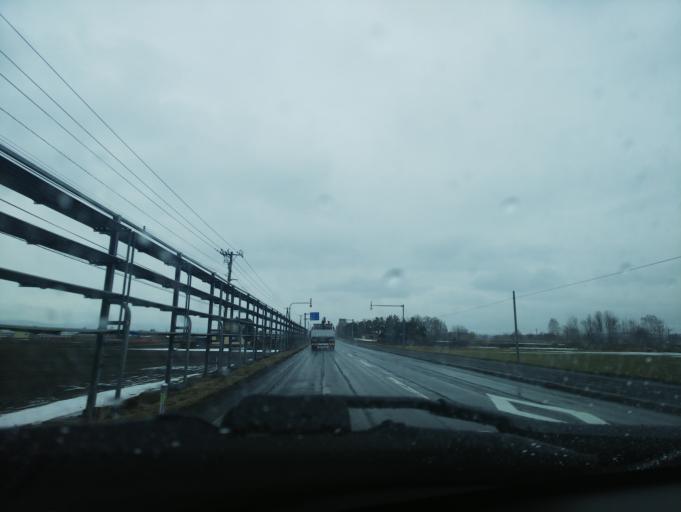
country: JP
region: Hokkaido
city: Nayoro
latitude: 44.2161
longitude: 142.3948
